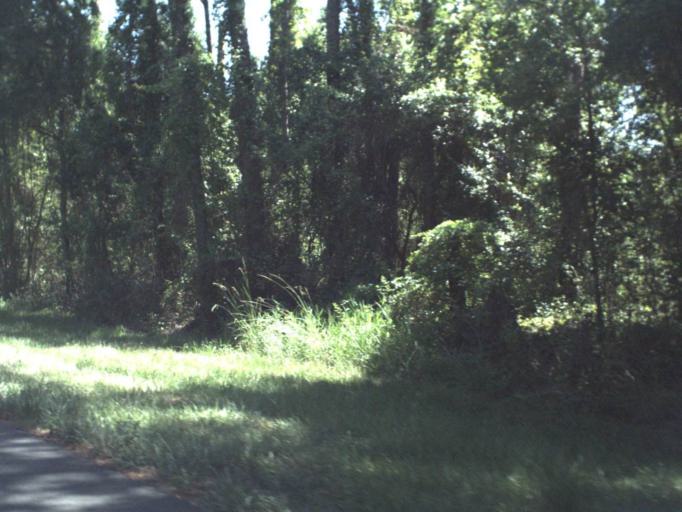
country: US
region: Florida
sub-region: Union County
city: Lake Butler
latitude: 30.0808
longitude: -82.2160
